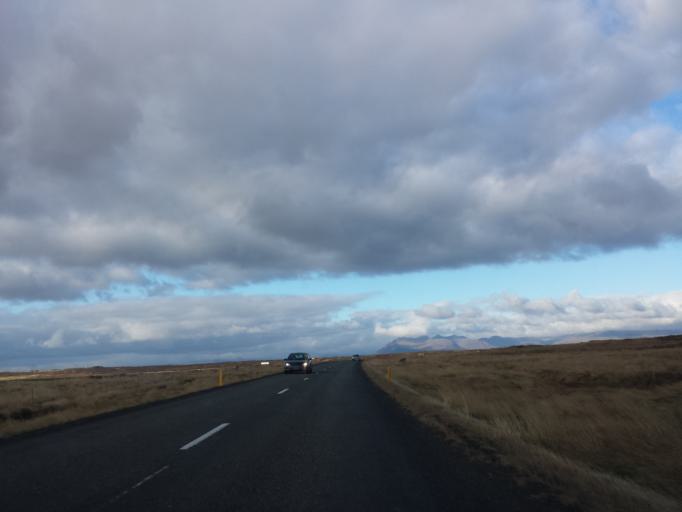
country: IS
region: West
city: Borgarnes
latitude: 64.7373
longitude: -22.1983
